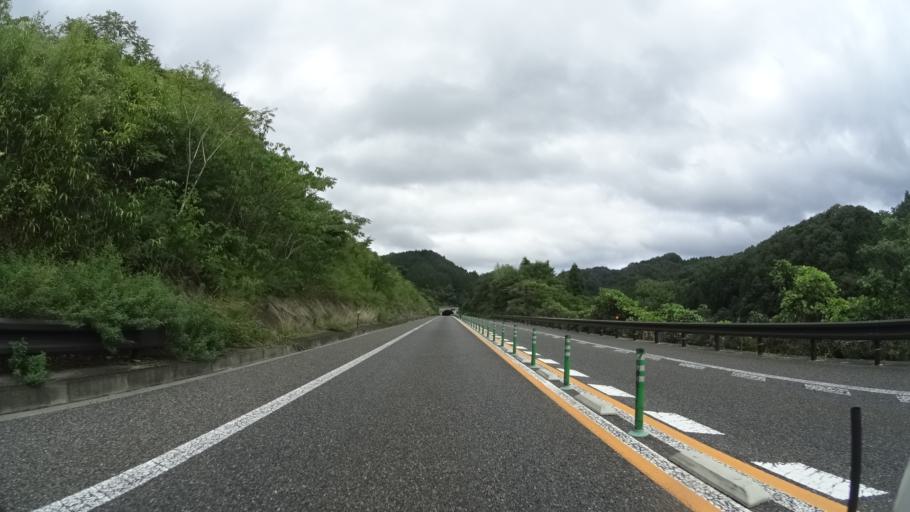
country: JP
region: Hyogo
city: Yamazakicho-nakabirose
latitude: 35.0771
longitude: 134.3455
